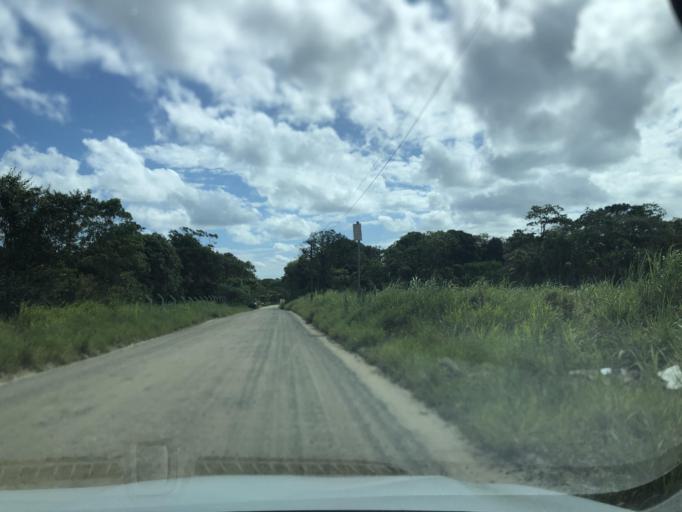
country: BR
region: Santa Catarina
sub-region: Sao Francisco Do Sul
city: Sao Francisco do Sul
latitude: -26.2244
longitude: -48.5783
